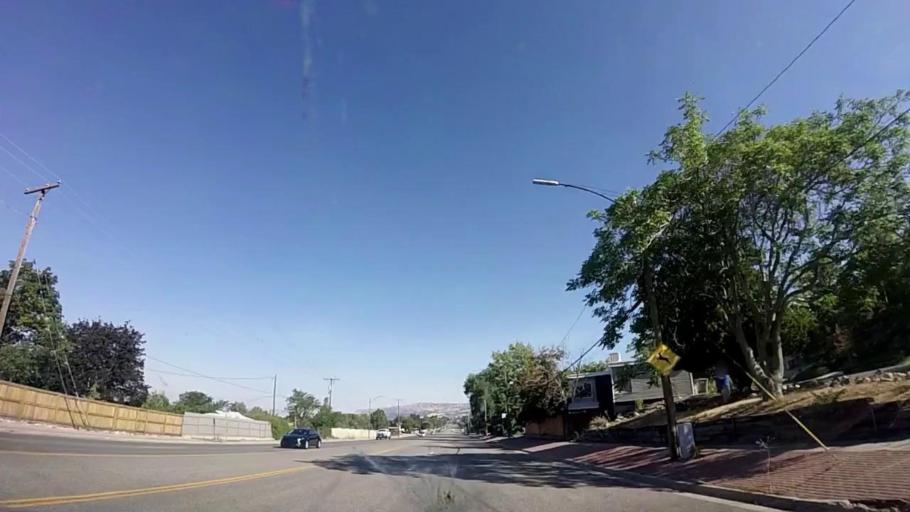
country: US
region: Utah
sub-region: Salt Lake County
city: Canyon Rim
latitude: 40.7263
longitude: -111.8151
